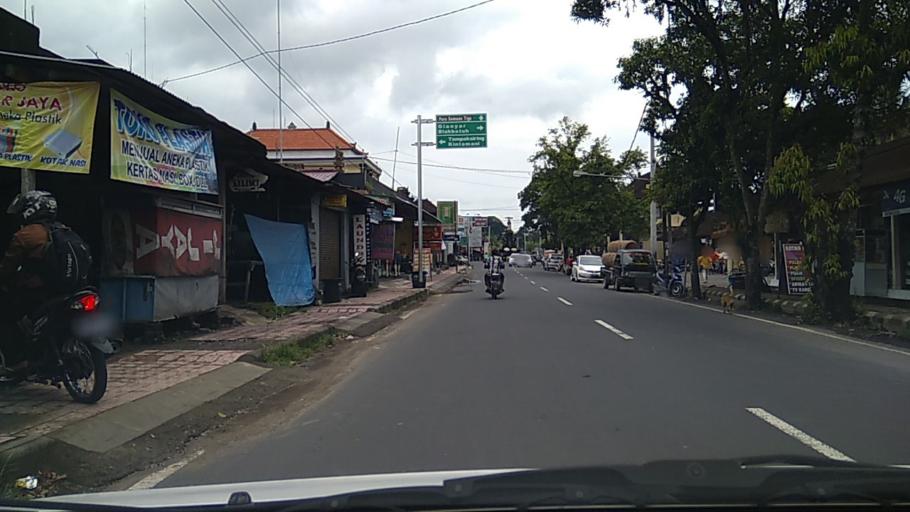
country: ID
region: Bali
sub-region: Kabupaten Gianyar
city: Ubud
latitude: -8.5236
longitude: 115.2910
